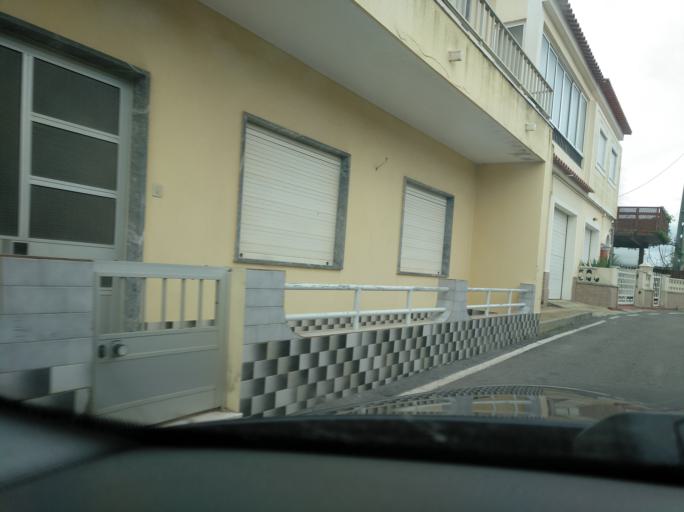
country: PT
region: Faro
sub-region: Vila Real de Santo Antonio
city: Monte Gordo
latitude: 37.1909
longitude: -7.5024
